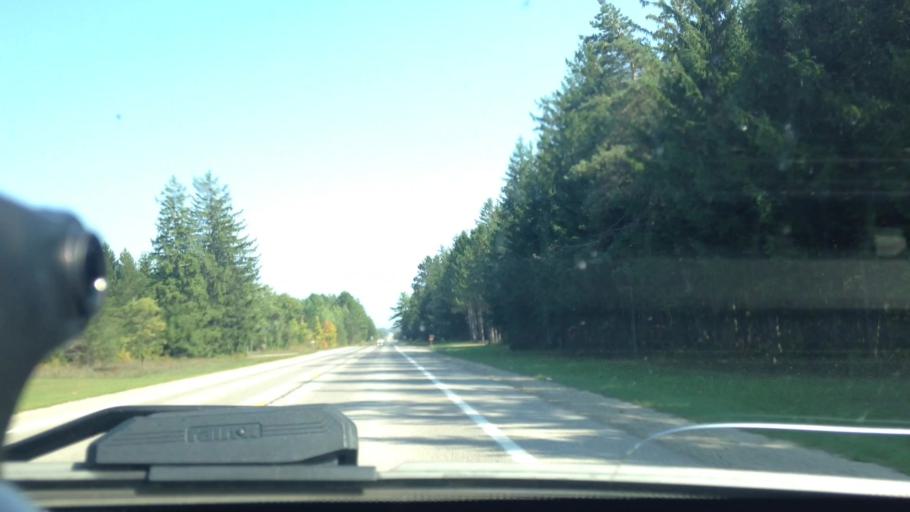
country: US
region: Michigan
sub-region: Luce County
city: Newberry
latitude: 46.3036
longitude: -85.4281
